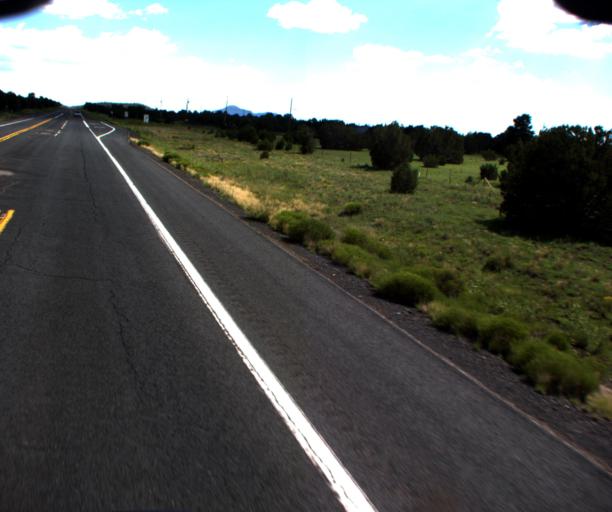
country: US
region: Arizona
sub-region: Coconino County
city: Williams
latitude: 35.3543
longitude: -112.1671
